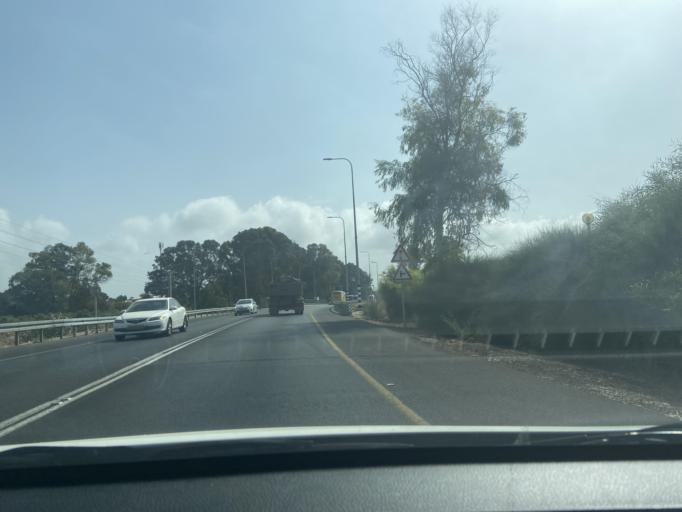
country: IL
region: Northern District
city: Nahariya
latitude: 33.0428
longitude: 35.1066
